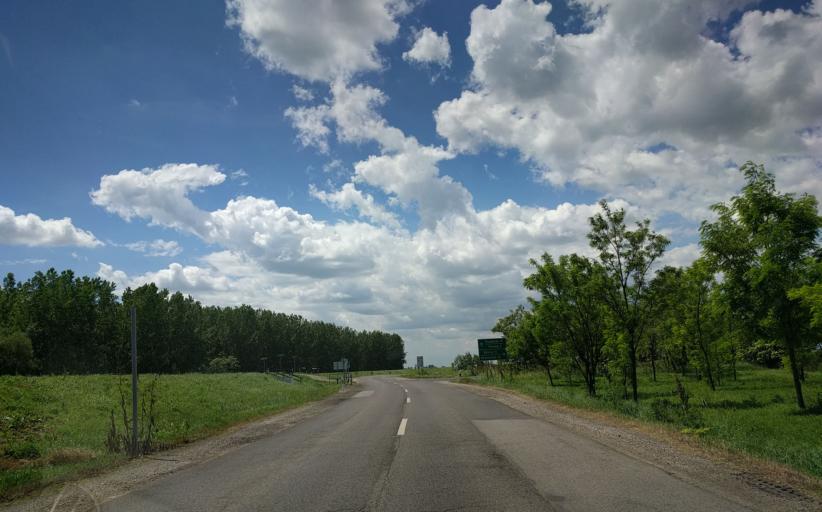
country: HU
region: Jasz-Nagykun-Szolnok
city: Toszeg
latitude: 47.1228
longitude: 20.1303
